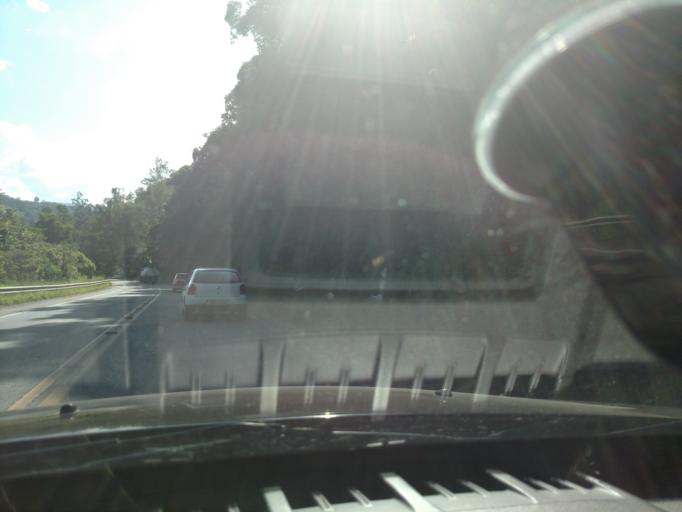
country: BR
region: Santa Catarina
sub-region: Ibirama
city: Ibirama
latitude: -27.0821
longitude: -49.5064
